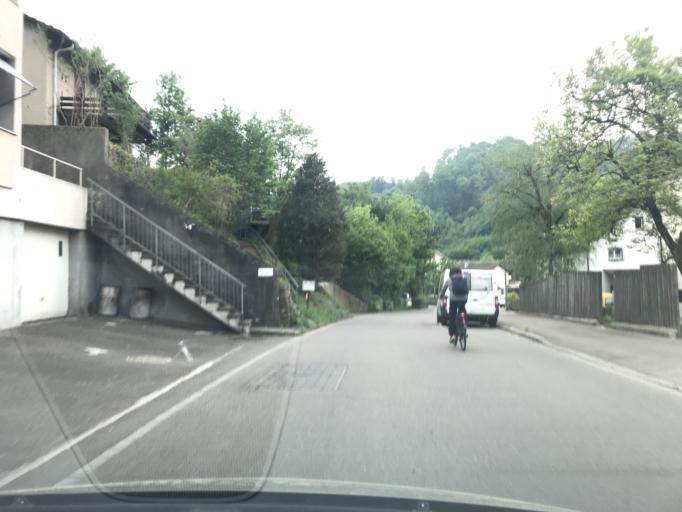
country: CH
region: Zurich
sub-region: Bezirk Winterthur
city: Wuelflingen (Kreis 6) / Lindenplatz
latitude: 47.5049
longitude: 8.6913
